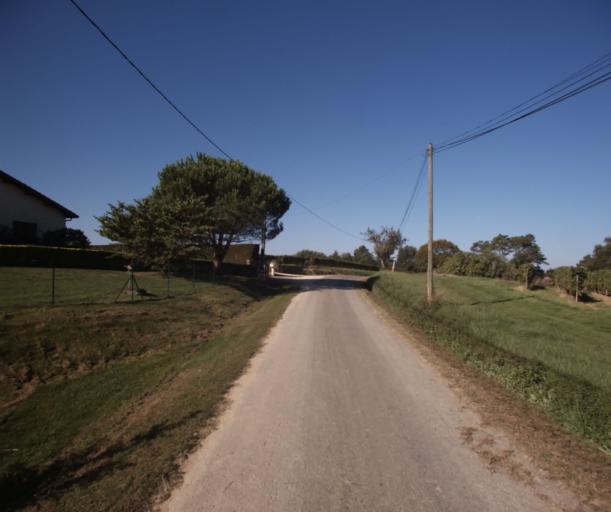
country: FR
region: Aquitaine
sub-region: Departement des Landes
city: Gabarret
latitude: 43.9062
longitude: 0.0185
